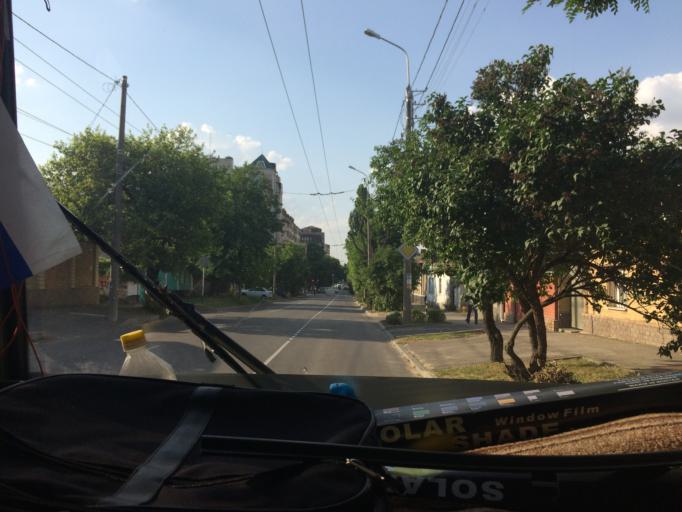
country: RU
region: Stavropol'skiy
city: Stavropol'
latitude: 45.0293
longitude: 41.9531
